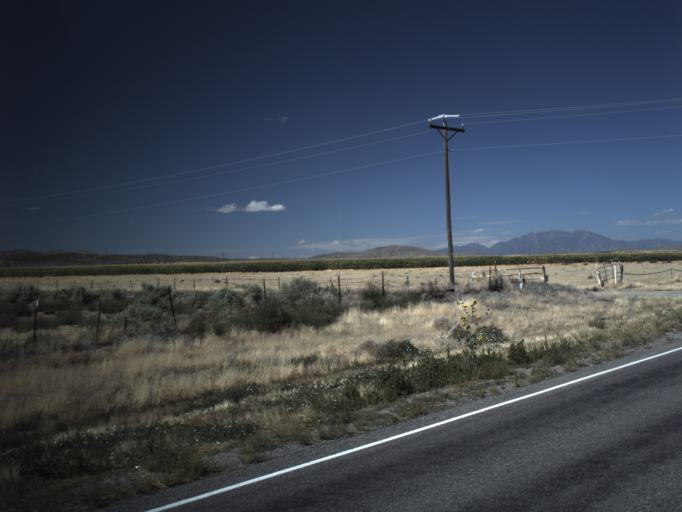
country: US
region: Utah
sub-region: Utah County
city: Genola
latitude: 40.0016
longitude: -111.9578
